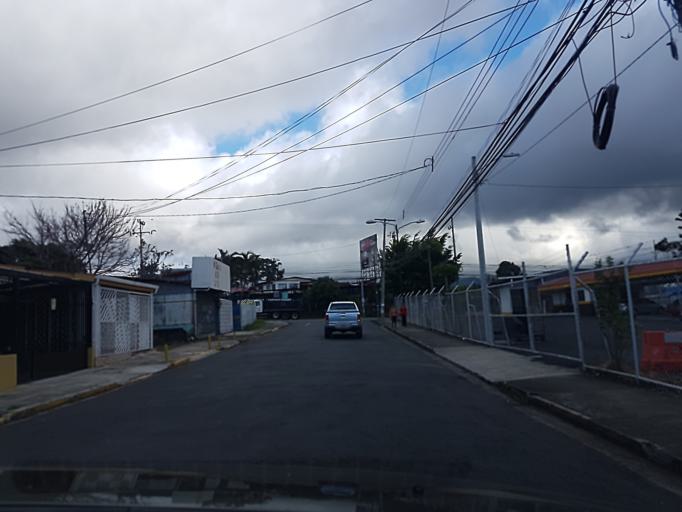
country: CR
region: San Jose
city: San Pedro
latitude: 9.9160
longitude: -84.0560
